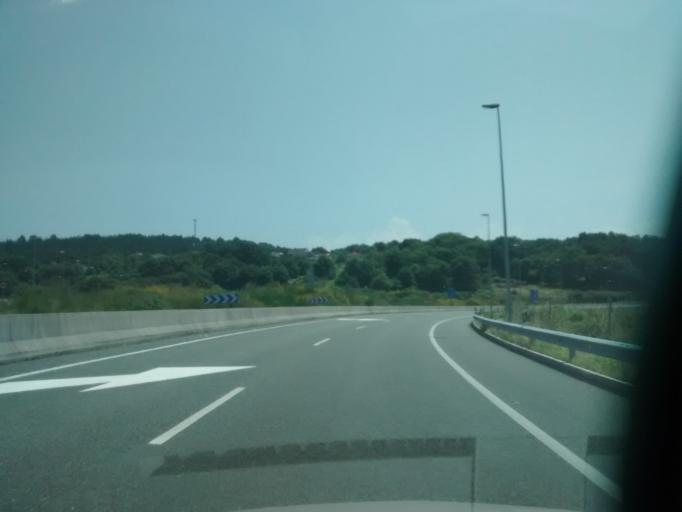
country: ES
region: Galicia
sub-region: Provincia de Ourense
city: Maside
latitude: 42.4071
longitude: -8.0134
